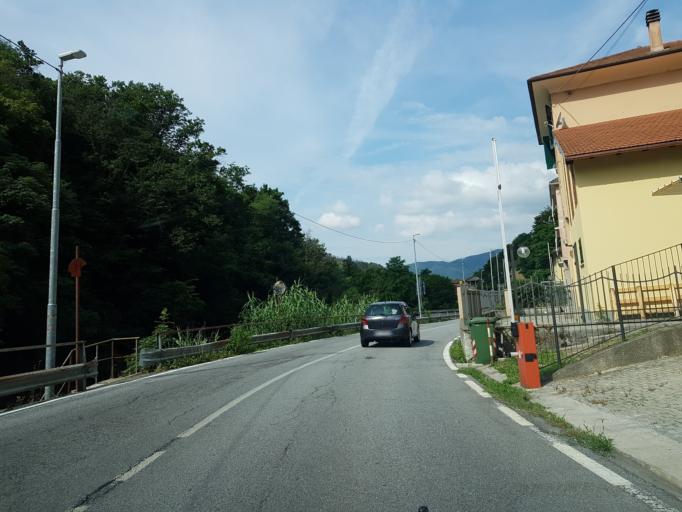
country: IT
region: Liguria
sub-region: Provincia di Genova
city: Manesseno
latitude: 44.4799
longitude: 8.9402
